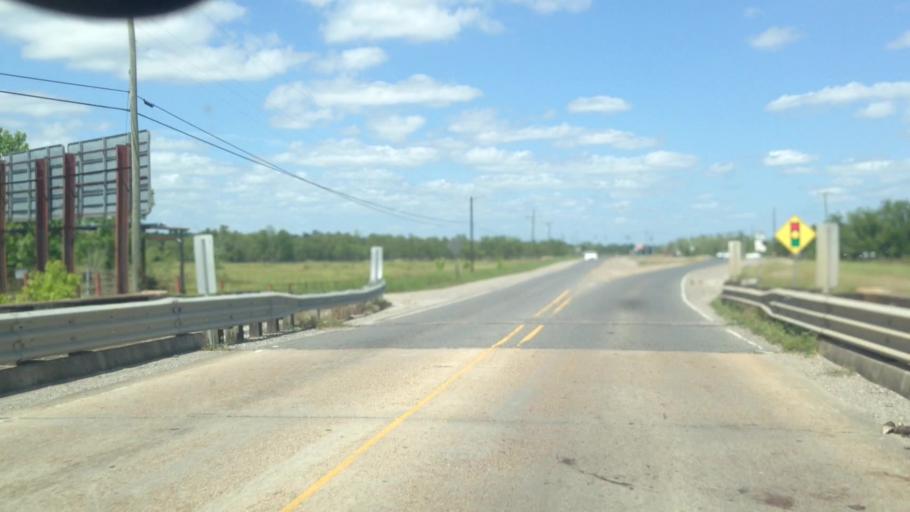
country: US
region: Louisiana
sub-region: Terrebonne Parish
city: Houma
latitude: 29.6531
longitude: -90.6809
